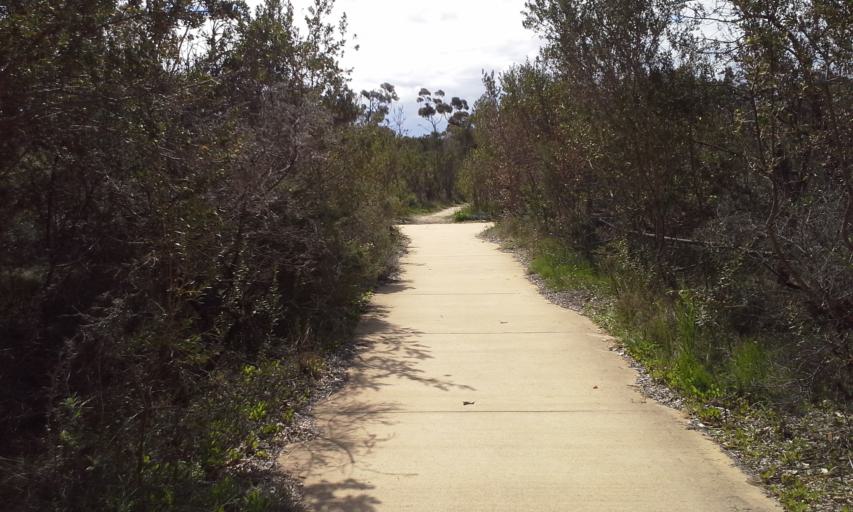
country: AU
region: Western Australia
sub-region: City of Perth
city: West Perth
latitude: -31.9630
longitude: 115.8366
